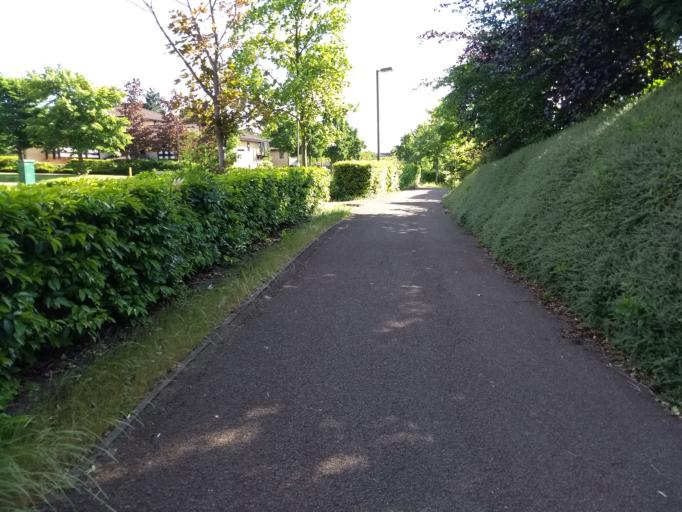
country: GB
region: England
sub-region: Milton Keynes
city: Shenley Church End
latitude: 52.0253
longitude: -0.7852
